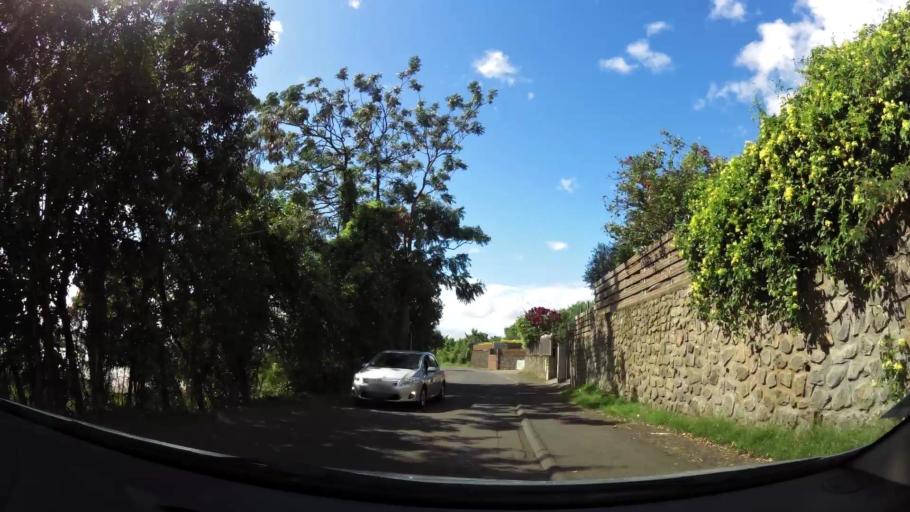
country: RE
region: Reunion
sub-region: Reunion
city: Sainte-Marie
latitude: -20.9184
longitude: 55.4985
